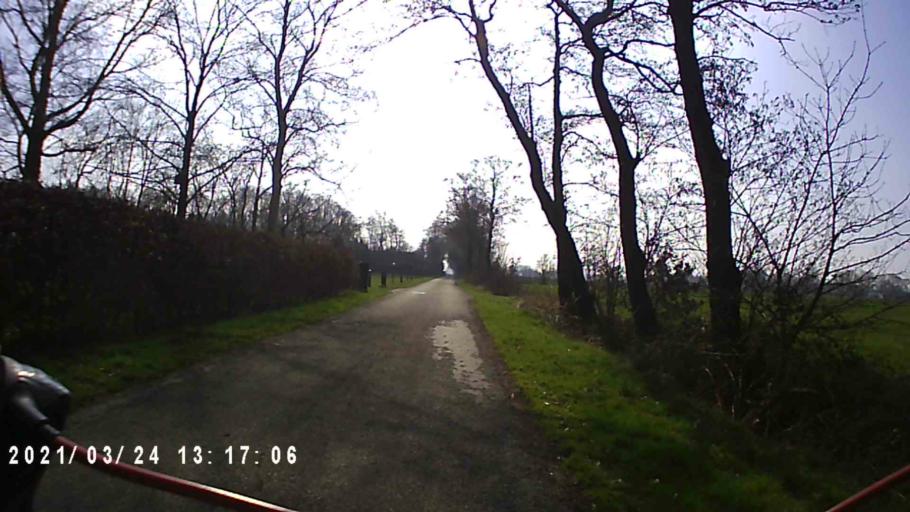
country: NL
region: Groningen
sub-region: Gemeente Leek
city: Leek
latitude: 53.1106
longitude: 6.2918
